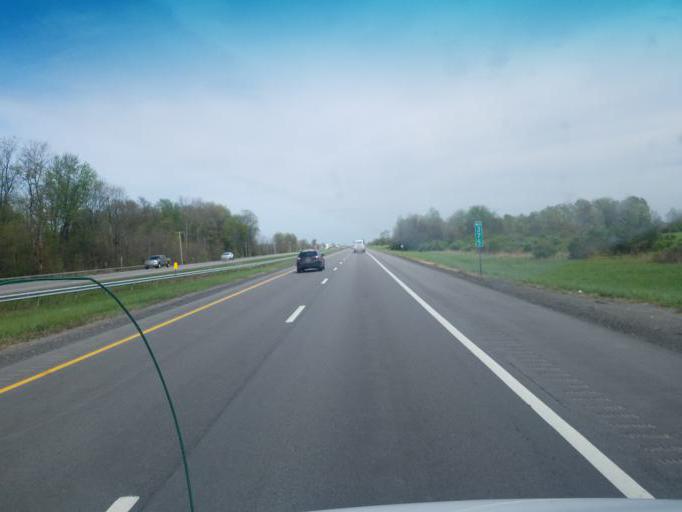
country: US
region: New York
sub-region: Livingston County
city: Caledonia
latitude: 43.0299
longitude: -77.8948
